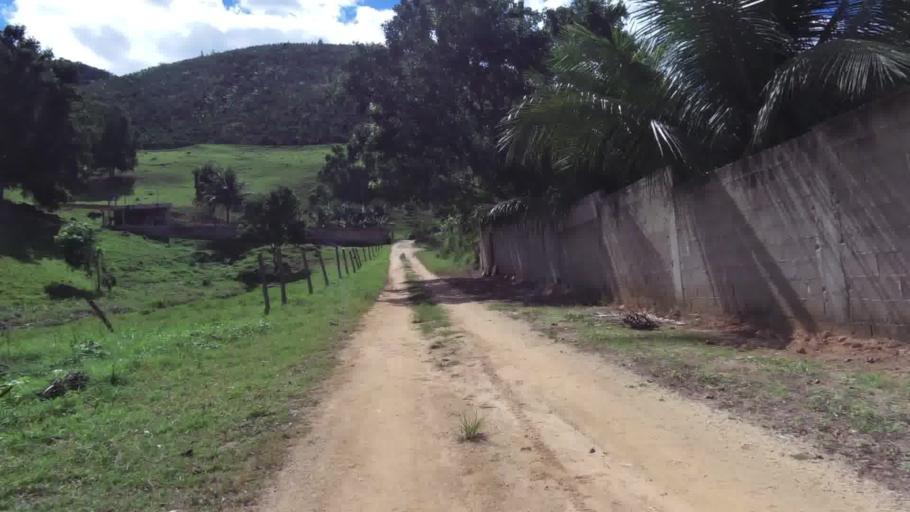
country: BR
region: Espirito Santo
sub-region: Rio Novo Do Sul
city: Rio Novo do Sul
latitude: -20.8607
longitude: -40.9494
